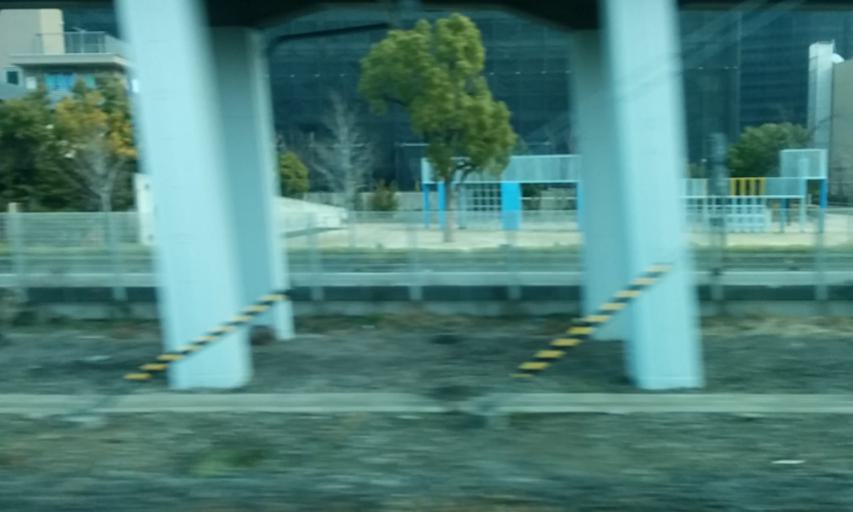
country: JP
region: Saitama
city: Kawaguchi
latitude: 35.8081
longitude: 139.7119
